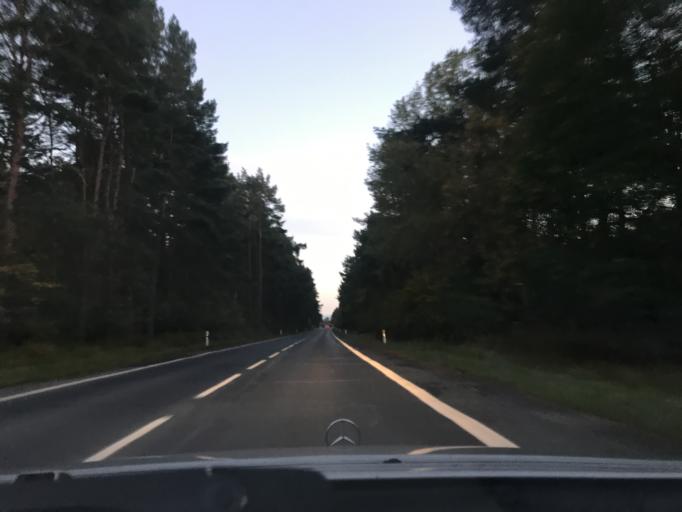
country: DE
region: Mecklenburg-Vorpommern
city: Karlshagen
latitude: 54.1253
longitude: 13.8244
